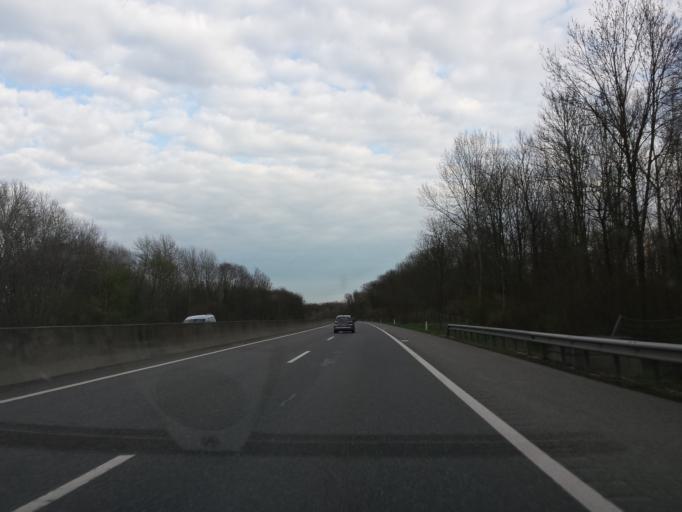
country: AT
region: Lower Austria
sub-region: Politischer Bezirk Tulln
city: Michelhausen
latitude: 48.3718
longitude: 15.9369
